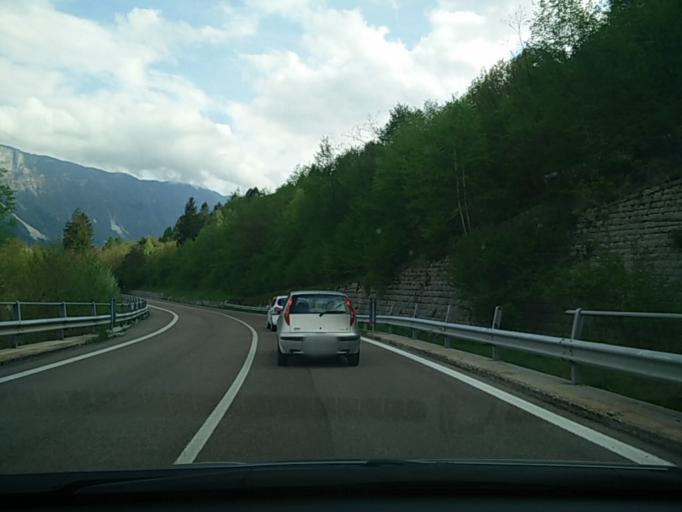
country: IT
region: Veneto
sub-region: Provincia di Belluno
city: Farra d'Alpago
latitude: 46.1116
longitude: 12.3258
